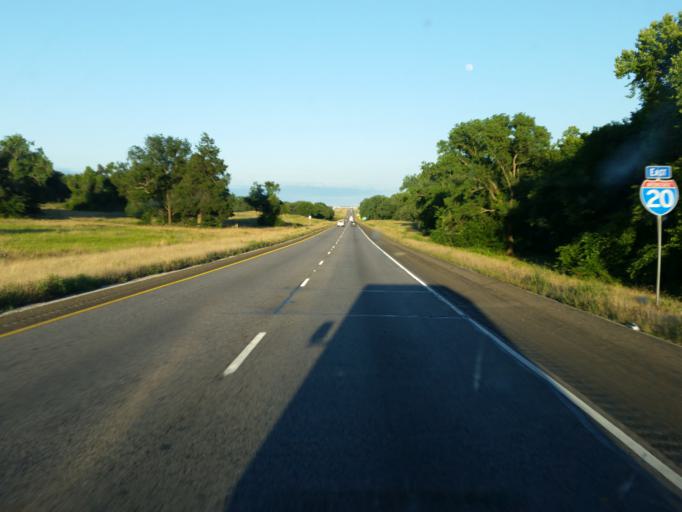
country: US
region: Texas
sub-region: Van Zandt County
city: Wills Point
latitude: 32.6632
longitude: -96.1256
